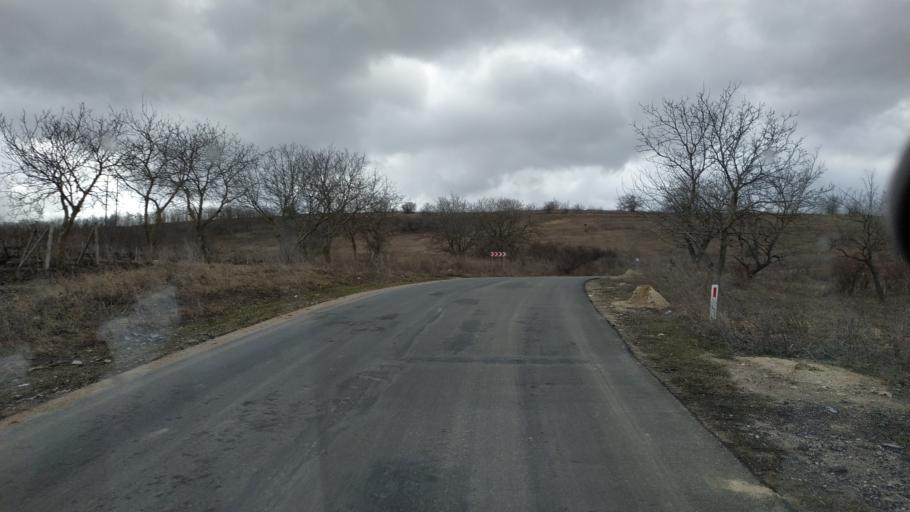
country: MD
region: Stinga Nistrului
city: Bucovat
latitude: 47.2214
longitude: 28.4250
